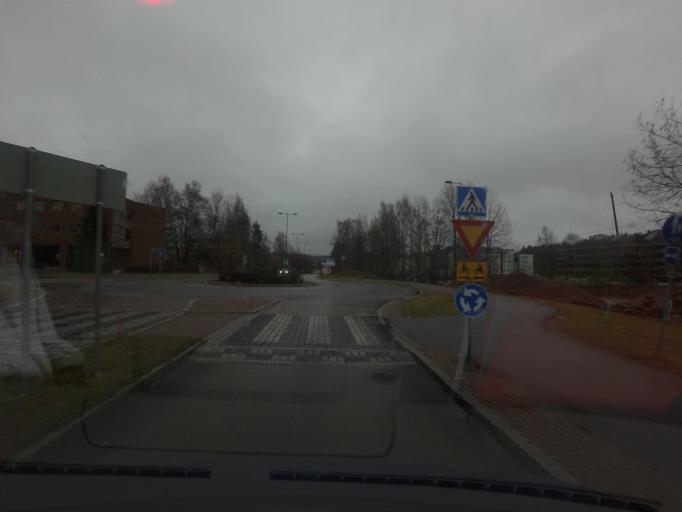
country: FI
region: Uusimaa
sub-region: Helsinki
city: Espoo
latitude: 60.2065
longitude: 24.6613
